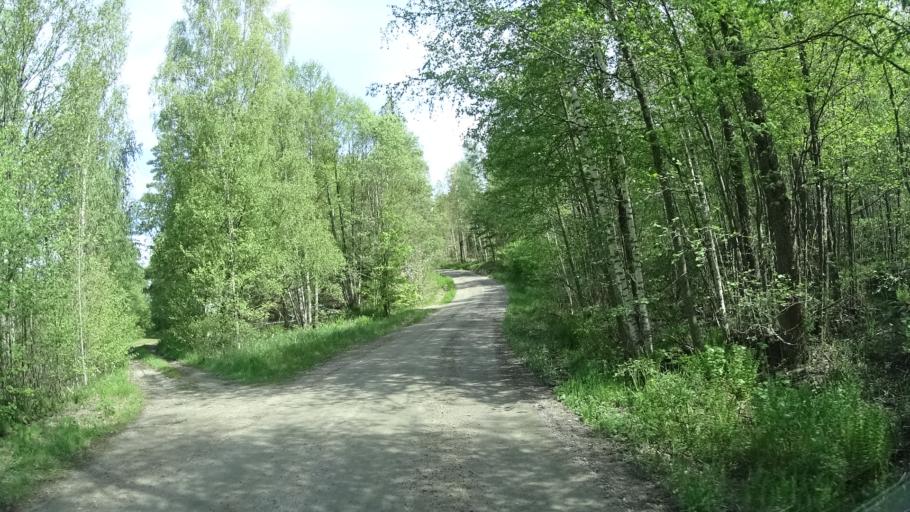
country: SE
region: OEstergoetland
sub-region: Finspangs Kommun
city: Finspang
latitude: 58.7506
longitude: 15.8295
